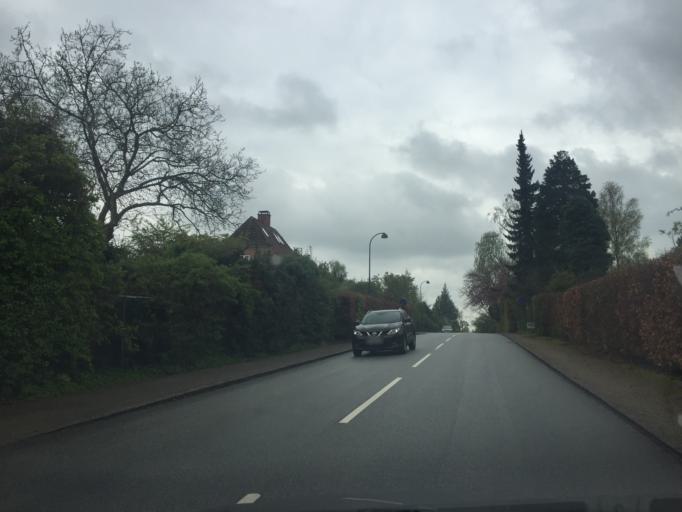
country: DK
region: Capital Region
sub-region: Rudersdal Kommune
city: Holte
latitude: 55.8077
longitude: 12.4488
